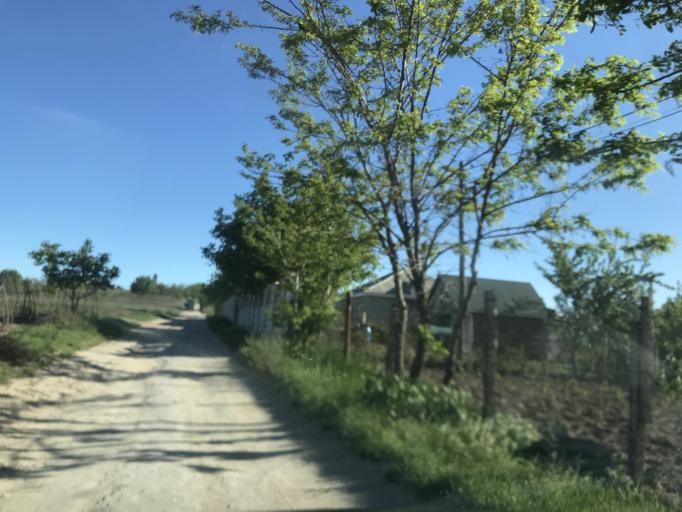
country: MD
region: Chisinau
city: Cricova
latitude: 47.2367
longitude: 28.8154
